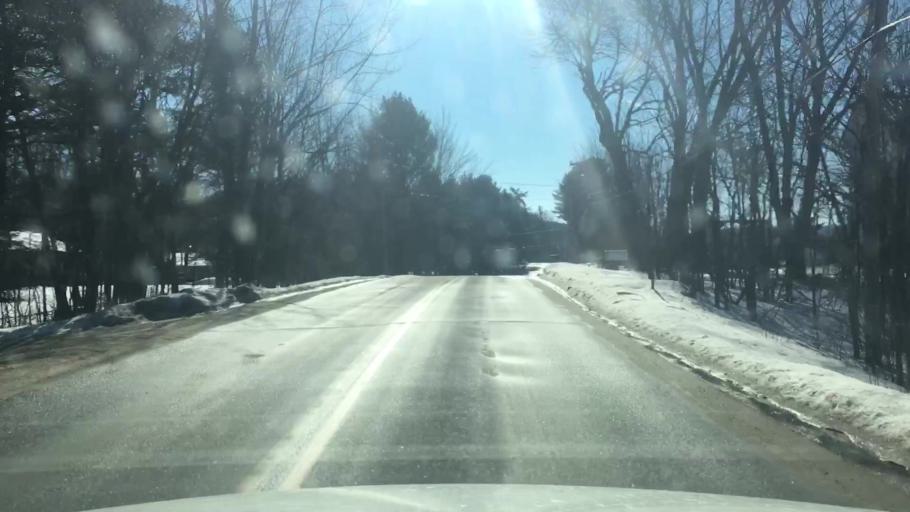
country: US
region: Maine
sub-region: Cumberland County
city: New Gloucester
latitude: 43.8742
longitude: -70.3334
